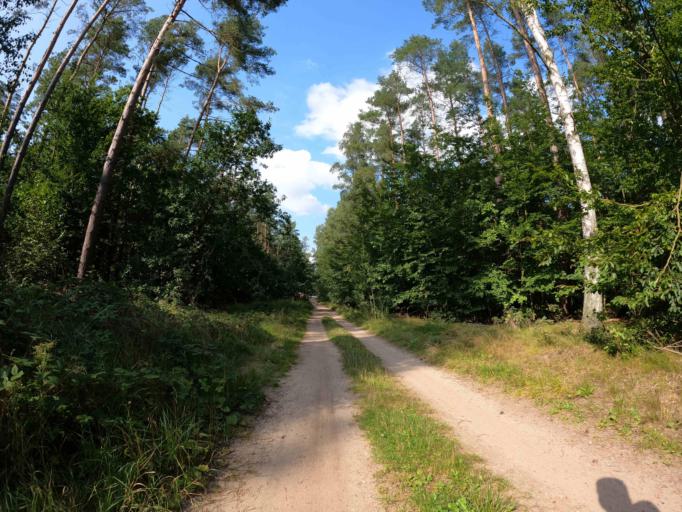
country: DE
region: Mecklenburg-Vorpommern
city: Malchow
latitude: 53.5281
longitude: 12.4709
